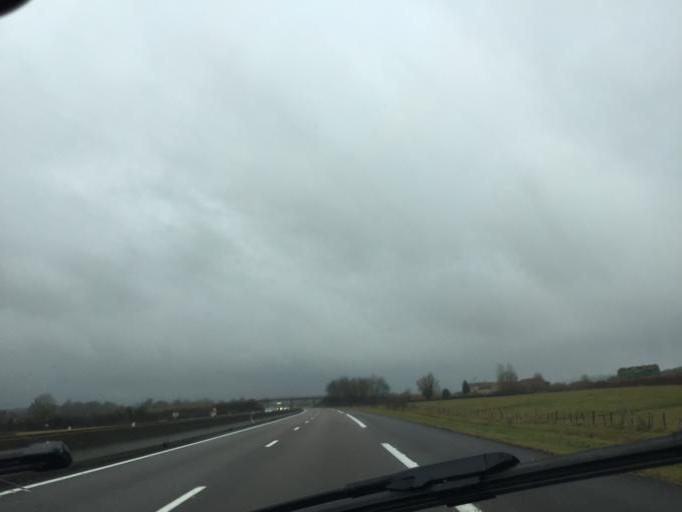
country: FR
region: Bourgogne
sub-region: Departement de la Cote-d'Or
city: Pouilly-en-Auxois
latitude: 47.2016
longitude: 4.6493
